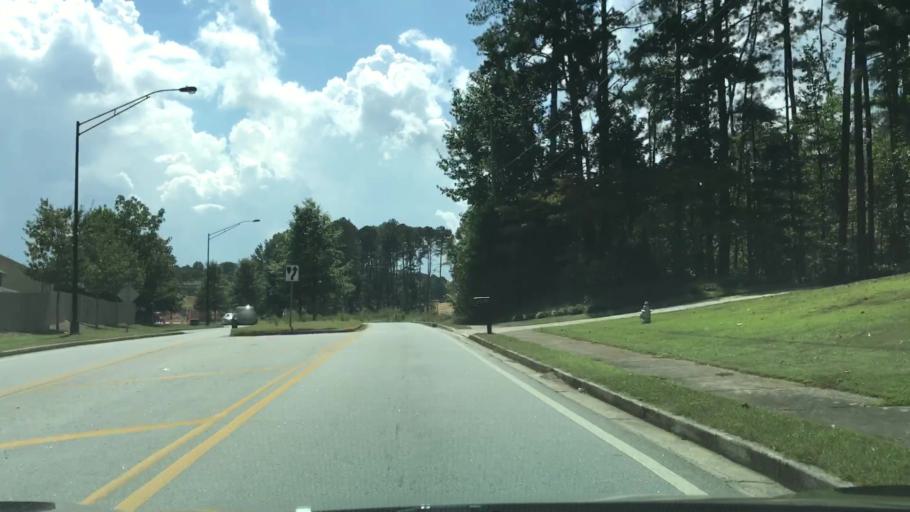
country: US
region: Georgia
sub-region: Gwinnett County
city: Snellville
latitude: 33.8546
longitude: -84.0474
